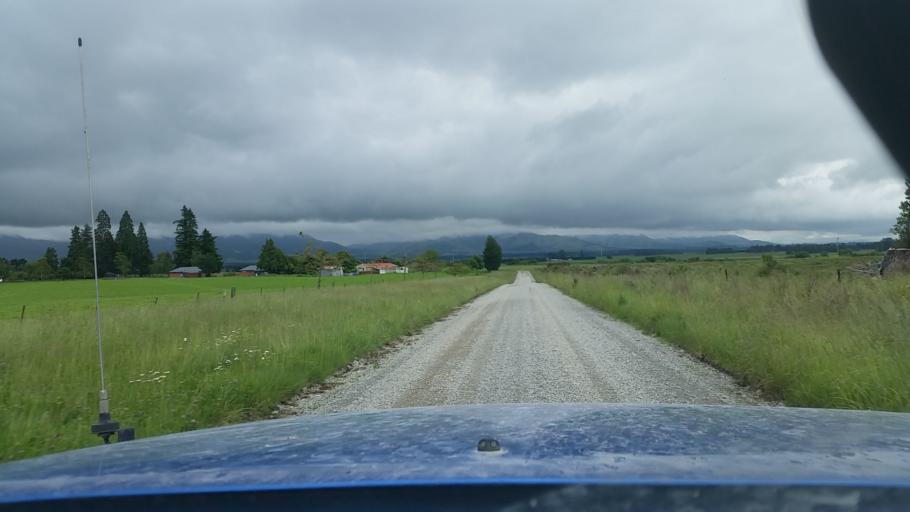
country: NZ
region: Canterbury
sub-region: Ashburton District
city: Methven
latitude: -43.6995
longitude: 171.4611
